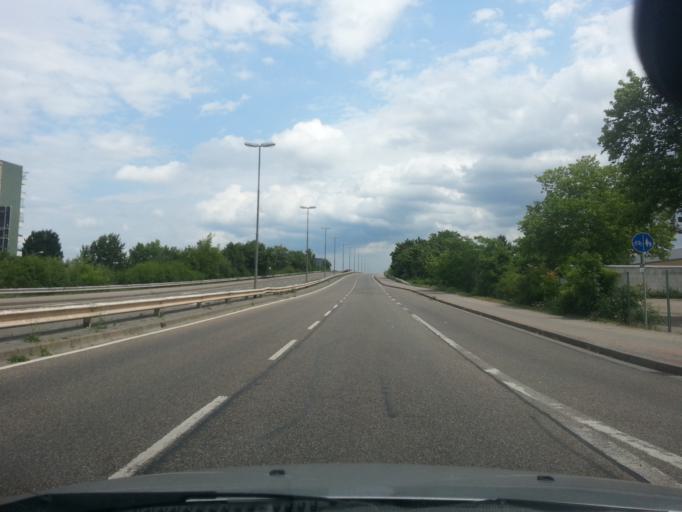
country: DE
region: Rheinland-Pfalz
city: Frankenthal
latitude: 49.5440
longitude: 8.3461
